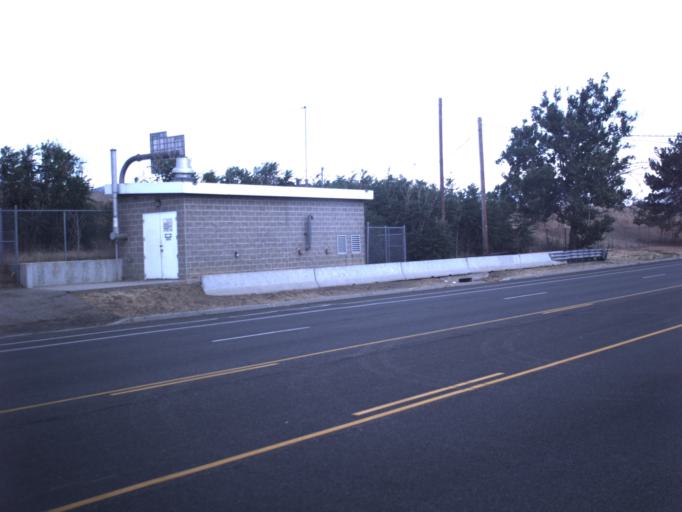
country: US
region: Utah
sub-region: Davis County
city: Sunset
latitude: 41.1441
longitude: -112.0262
